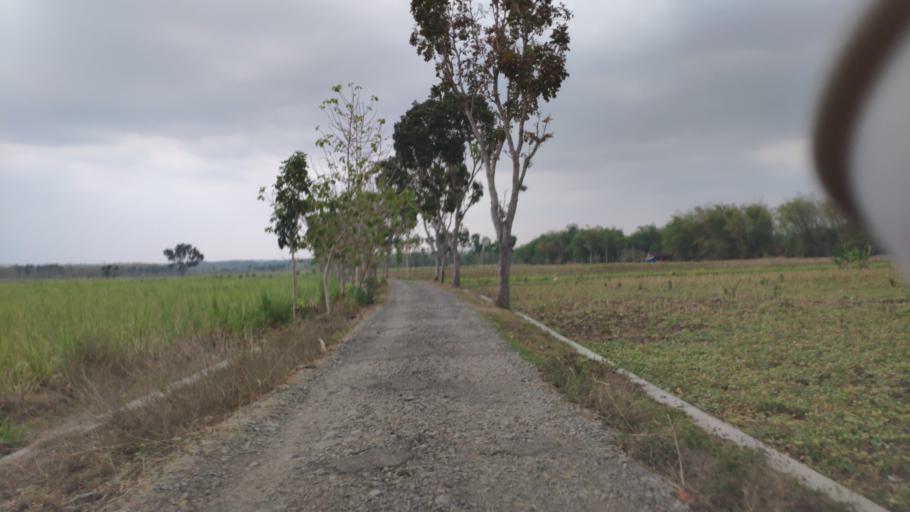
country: ID
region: Central Java
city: Kalangan
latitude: -6.9433
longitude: 111.3646
